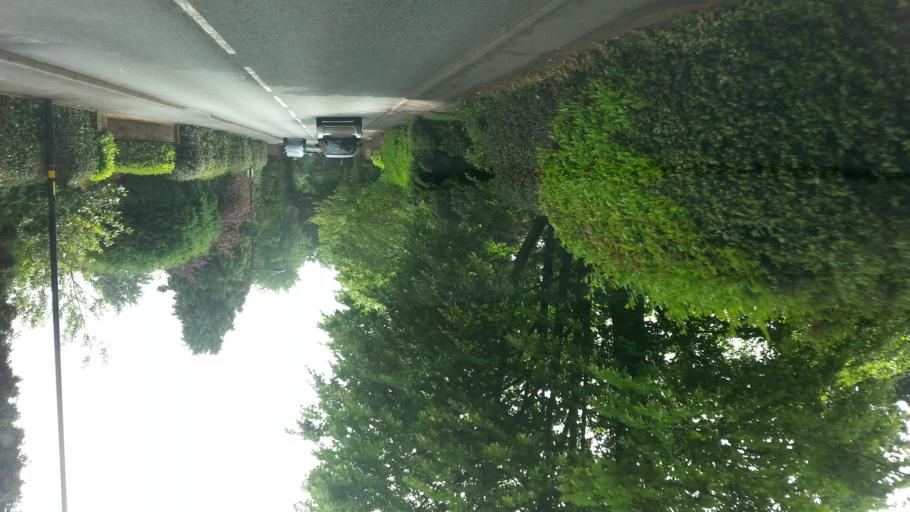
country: GB
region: England
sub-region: City and Borough of Birmingham
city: Sutton Coldfield
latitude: 52.5816
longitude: -1.8324
